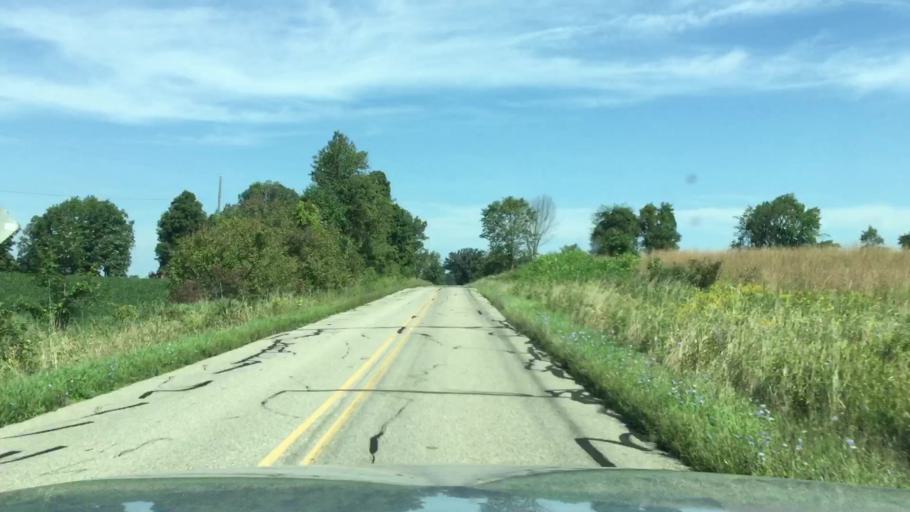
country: US
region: Michigan
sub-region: Lenawee County
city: Manitou Beach-Devils Lake
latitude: 41.9994
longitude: -84.3202
